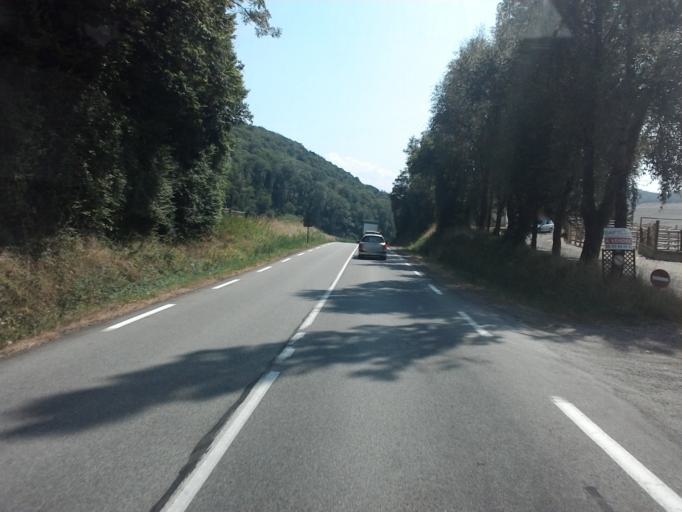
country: FR
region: Rhone-Alpes
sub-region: Departement de l'Isere
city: Bilieu
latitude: 45.4515
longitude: 5.5672
